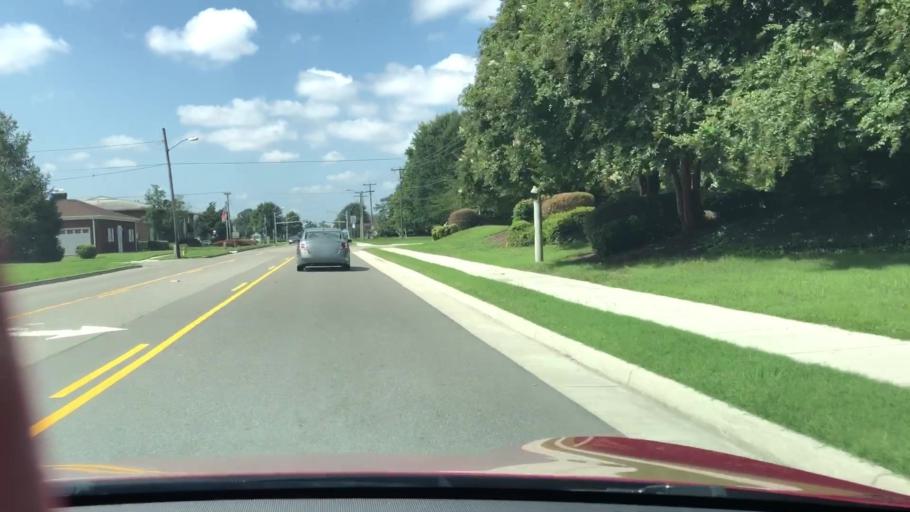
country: US
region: Virginia
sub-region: City of Norfolk
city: Norfolk
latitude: 36.8654
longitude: -76.2061
